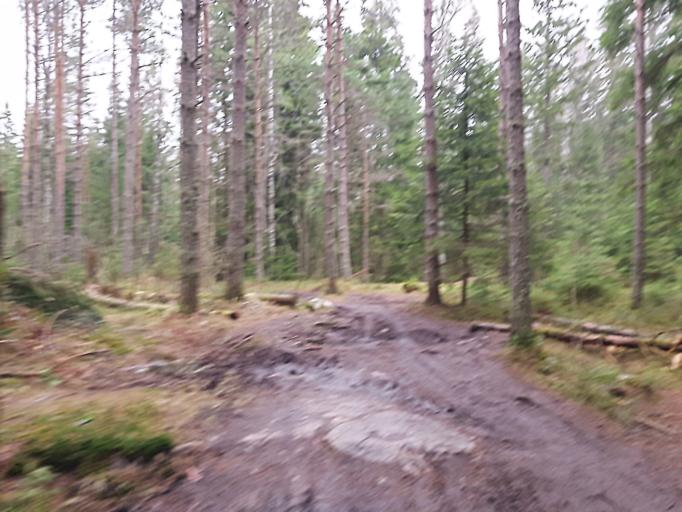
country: FI
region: Uusimaa
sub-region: Helsinki
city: Helsinki
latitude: 60.2616
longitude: 24.9213
